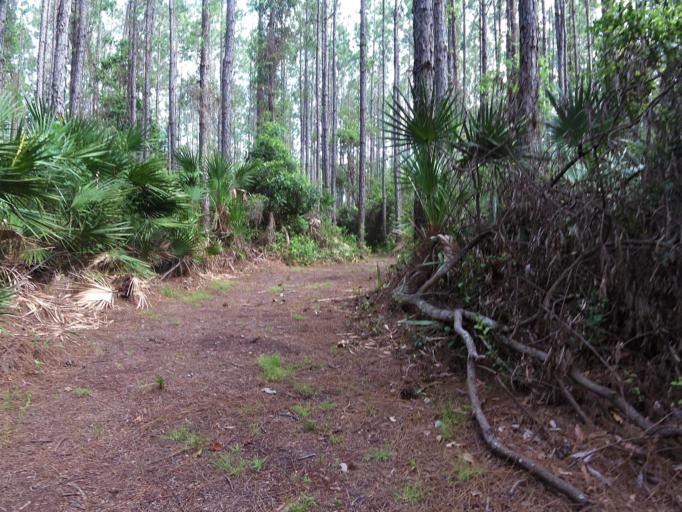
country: US
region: Florida
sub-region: Duval County
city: Atlantic Beach
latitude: 30.4552
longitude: -81.4732
